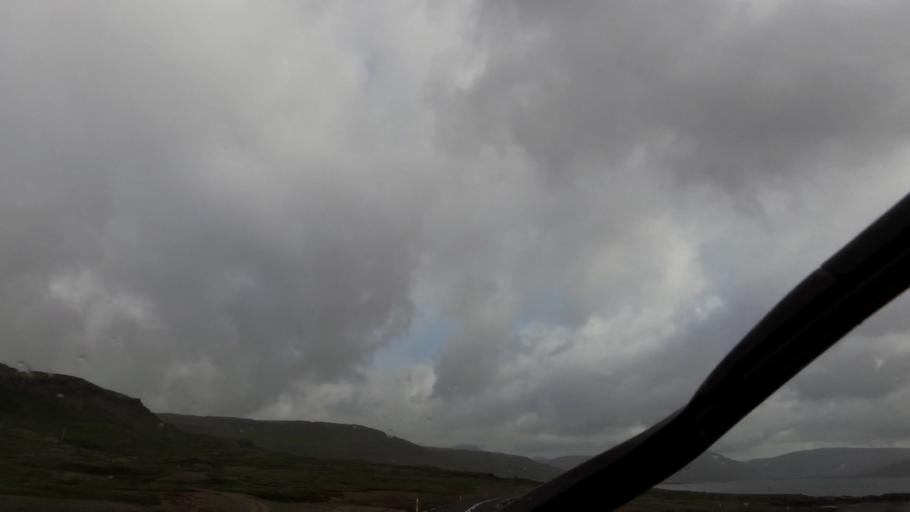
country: IS
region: Westfjords
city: Isafjoerdur
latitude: 65.5376
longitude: -23.2003
